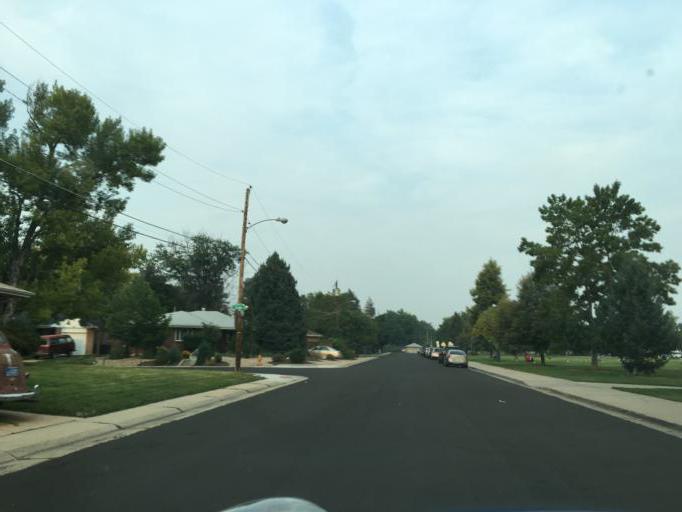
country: US
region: Colorado
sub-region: Arapahoe County
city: Glendale
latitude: 39.6859
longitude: -104.9249
